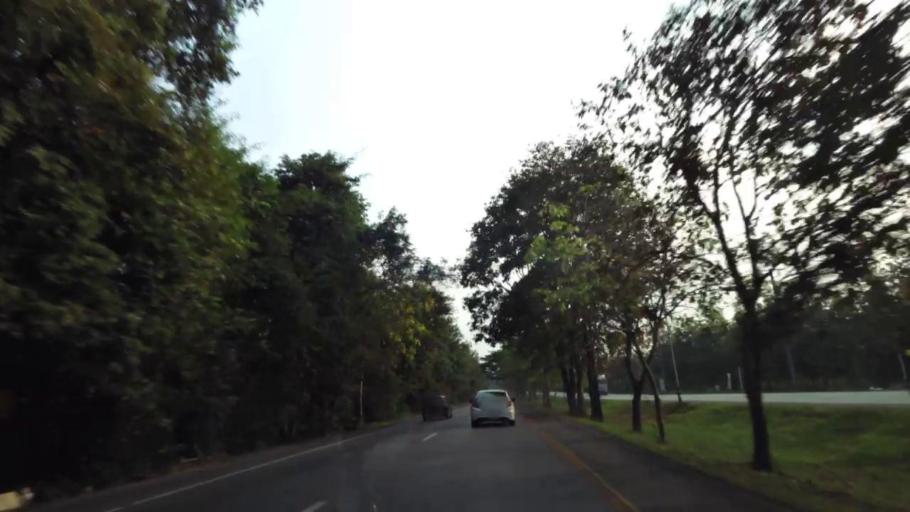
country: TH
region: Chanthaburi
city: Chanthaburi
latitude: 12.5370
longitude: 102.1577
